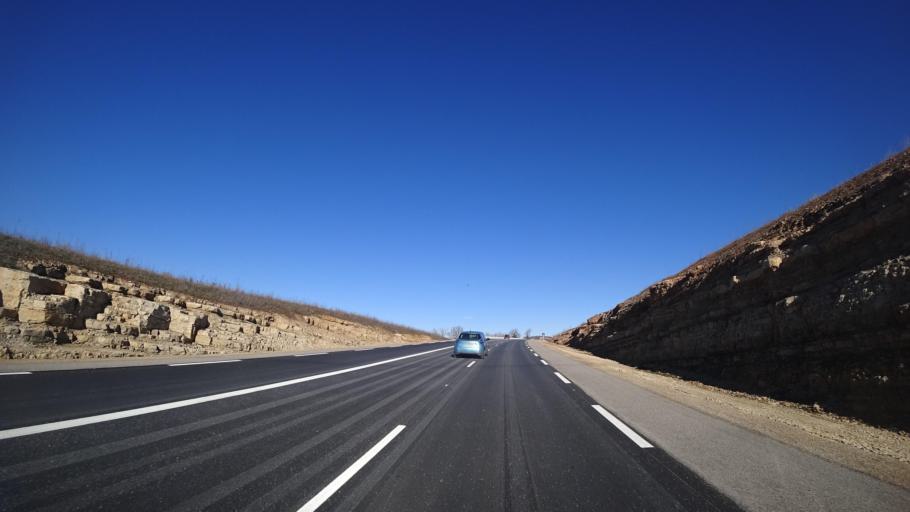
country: FR
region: Midi-Pyrenees
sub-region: Departement de l'Aveyron
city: Sebazac-Concoures
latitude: 44.3896
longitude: 2.6137
